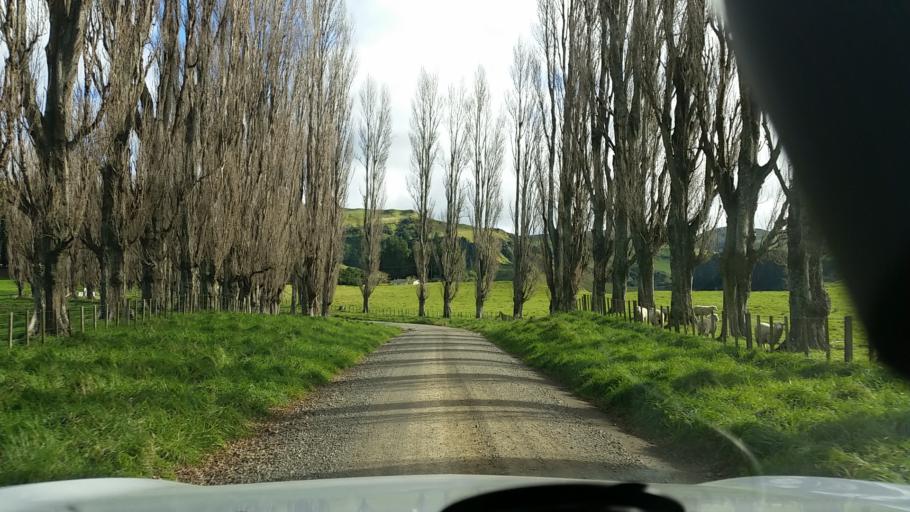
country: NZ
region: Hawke's Bay
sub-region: Napier City
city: Napier
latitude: -39.1011
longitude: 176.8785
